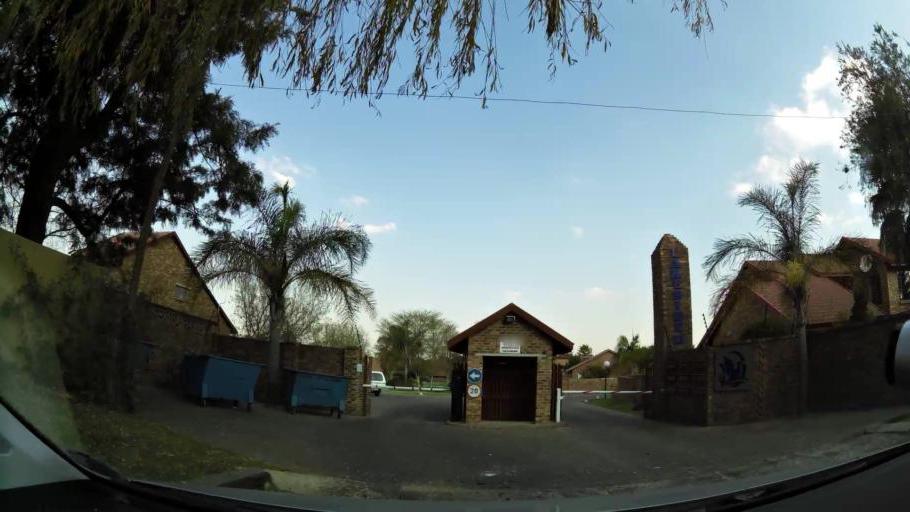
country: ZA
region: Gauteng
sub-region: City of Johannesburg Metropolitan Municipality
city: Modderfontein
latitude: -26.0830
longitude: 28.2011
